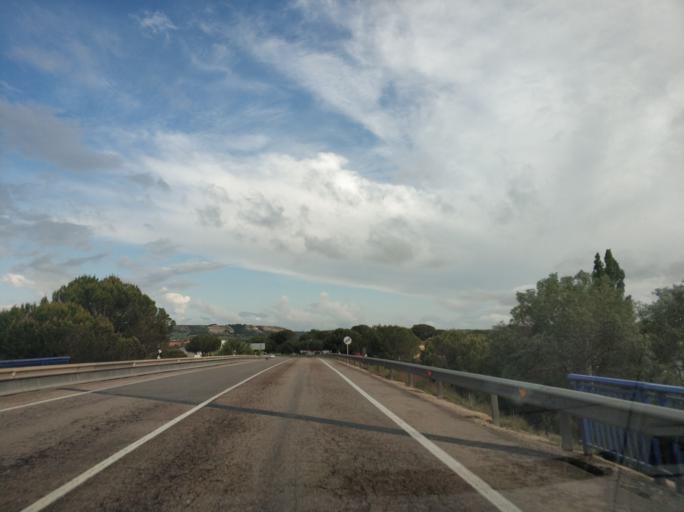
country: ES
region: Castille and Leon
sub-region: Provincia de Valladolid
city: Penafiel
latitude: 41.6064
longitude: -4.1410
